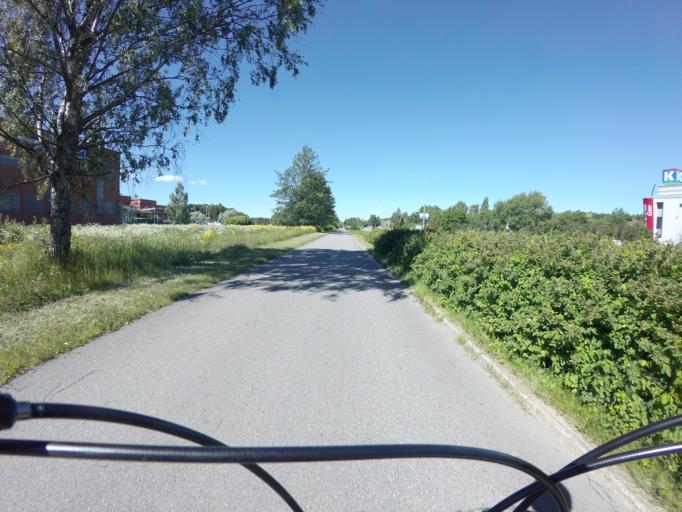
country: FI
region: Varsinais-Suomi
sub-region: Turku
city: Turku
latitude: 60.4566
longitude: 22.2337
